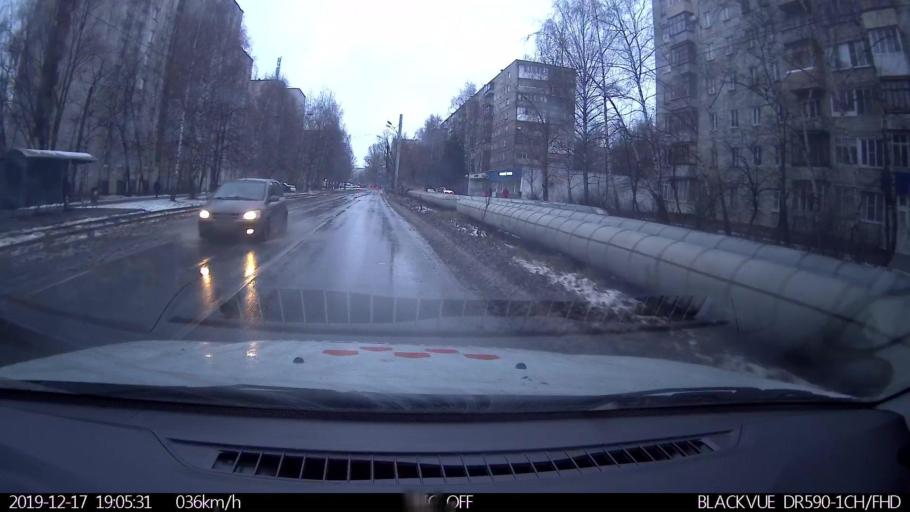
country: RU
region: Nizjnij Novgorod
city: Nizhniy Novgorod
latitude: 56.3342
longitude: 43.8736
